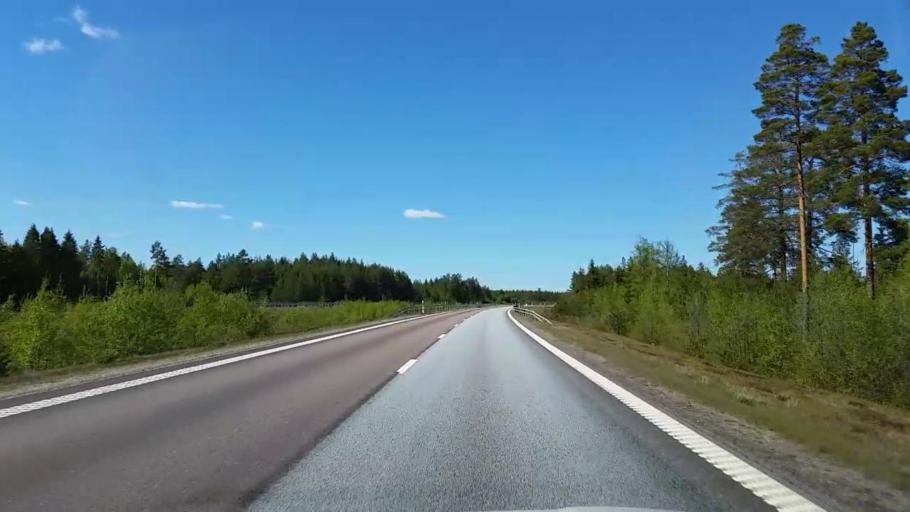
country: SE
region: Gaevleborg
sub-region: Soderhamns Kommun
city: Soderhamn
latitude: 61.3792
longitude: 16.9948
